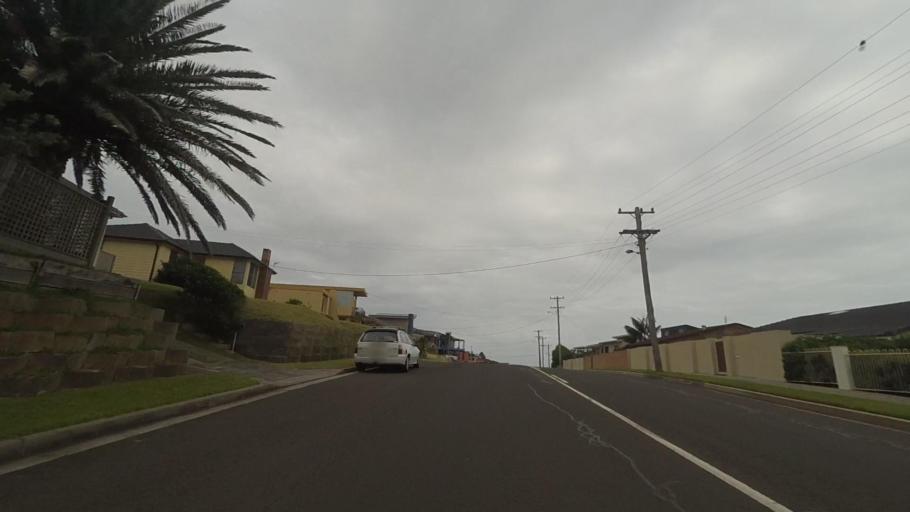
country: AU
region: New South Wales
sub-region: Wollongong
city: Port Kembla
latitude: -34.4897
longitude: 150.9051
